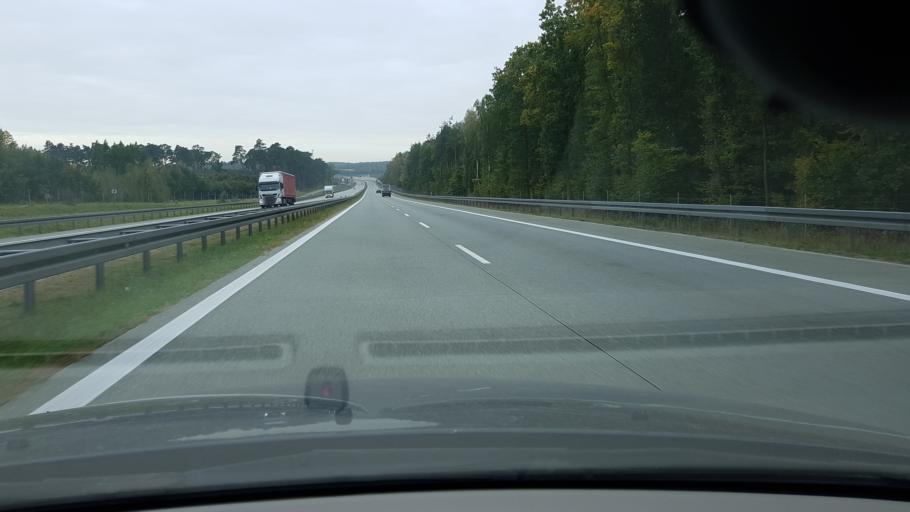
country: PL
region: Lodz Voivodeship
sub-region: Powiat rawski
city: Regnow
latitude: 51.8327
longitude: 20.3359
